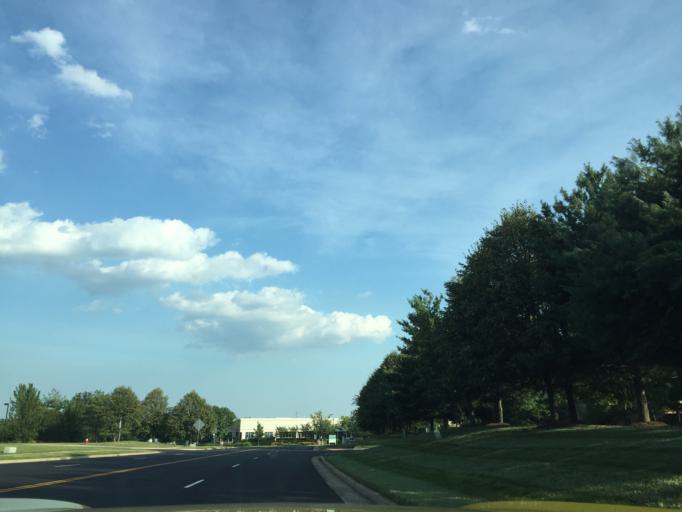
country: US
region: Virginia
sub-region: Loudoun County
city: Sterling
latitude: 39.0221
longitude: -77.4561
